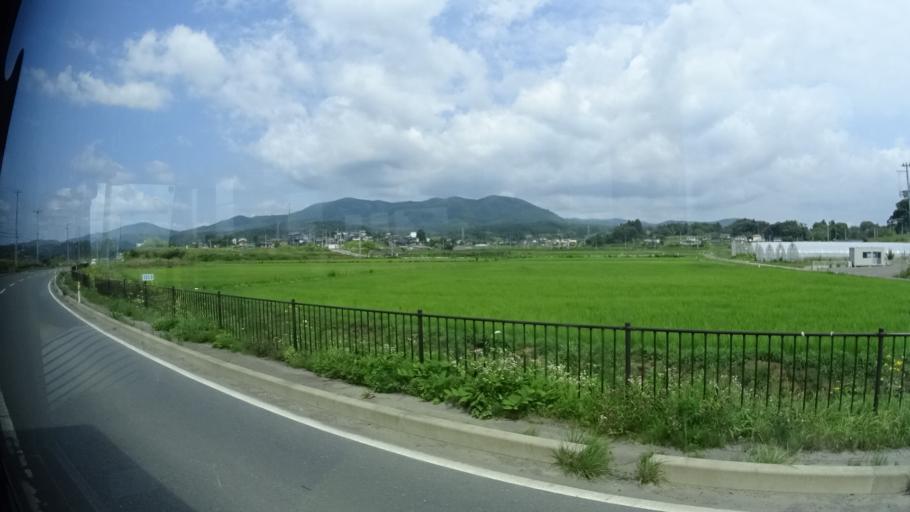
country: JP
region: Iwate
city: Ofunato
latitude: 38.8141
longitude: 141.5720
